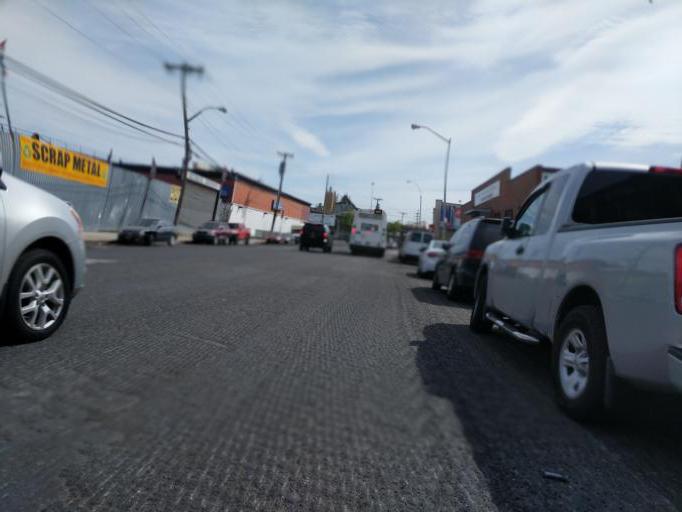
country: US
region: New York
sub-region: Queens County
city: Jamaica
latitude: 40.7050
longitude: -73.7837
